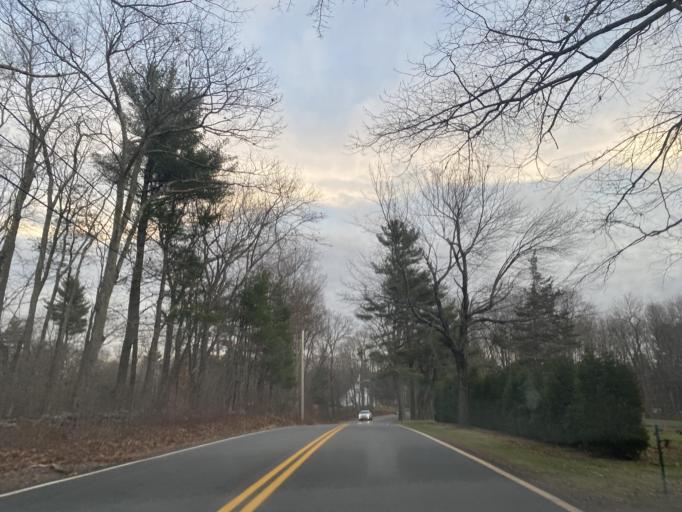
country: US
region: Massachusetts
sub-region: Worcester County
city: Paxton
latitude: 42.2800
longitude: -71.9206
